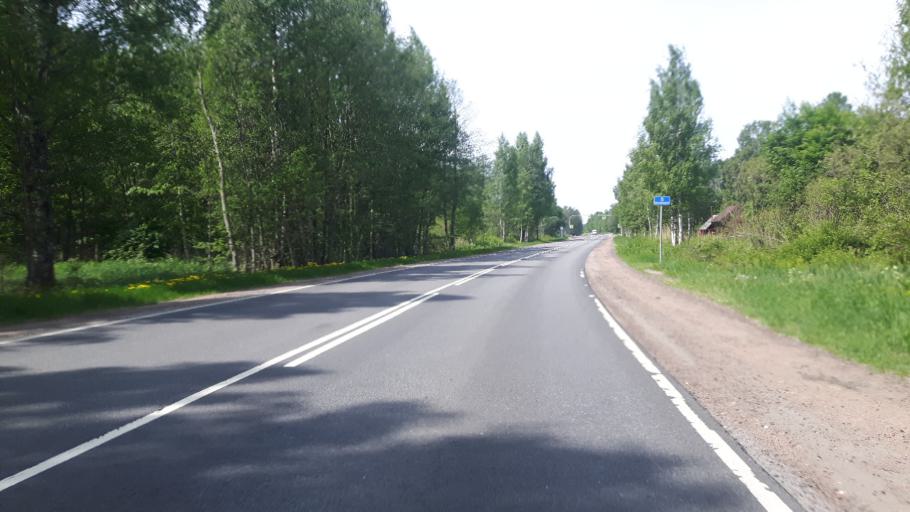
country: RU
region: Leningrad
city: Ust'-Luga
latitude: 59.6505
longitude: 28.3634
